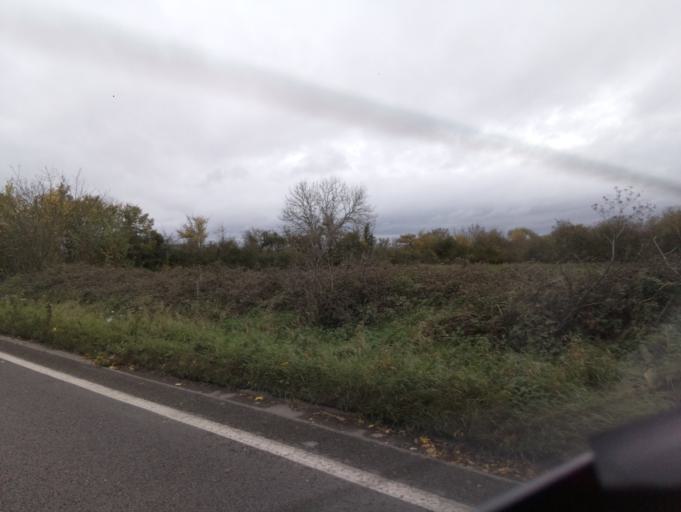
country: GB
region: England
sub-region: Somerset
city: Ilchester
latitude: 51.0229
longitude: -2.6383
